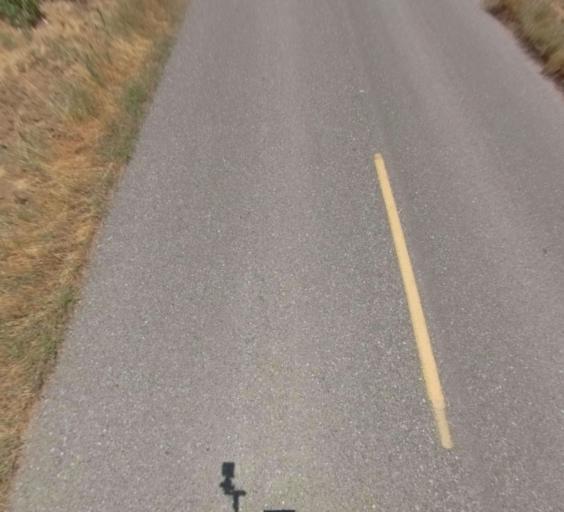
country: US
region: California
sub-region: Madera County
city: Madera Acres
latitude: 37.0548
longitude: -120.0111
